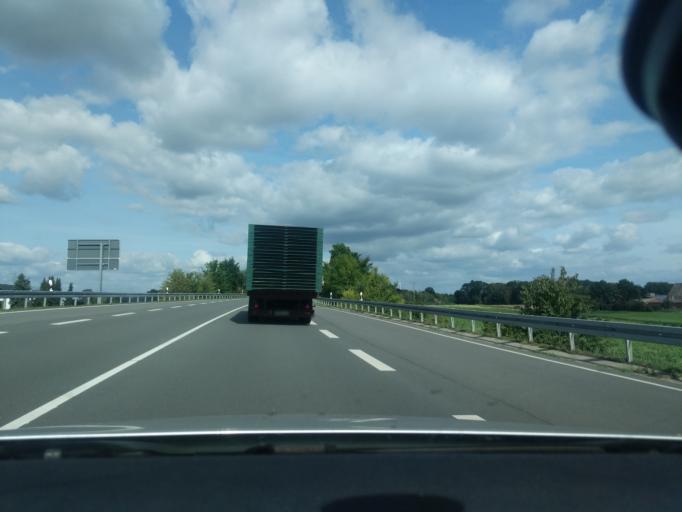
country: DE
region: Lower Saxony
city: Bohmte
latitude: 52.3700
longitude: 8.2998
